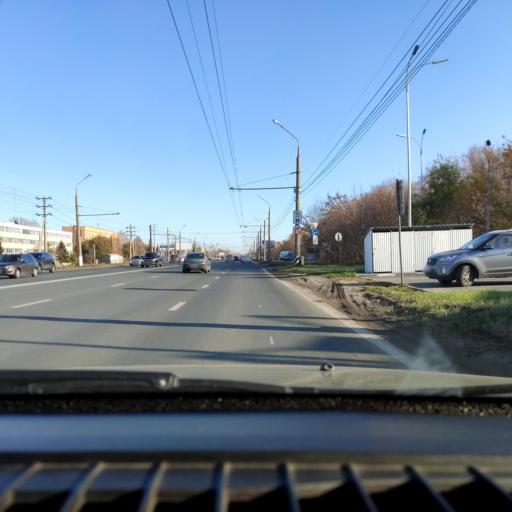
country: RU
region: Samara
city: Tol'yatti
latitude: 53.5527
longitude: 49.2948
